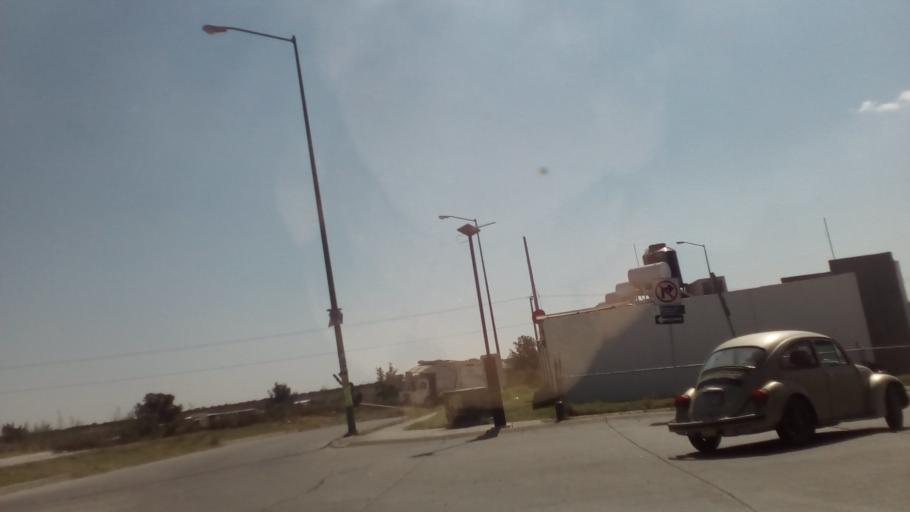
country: MX
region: Guanajuato
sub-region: Leon
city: Fraccionamiento Paseo de las Torres
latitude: 21.1871
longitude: -101.7644
